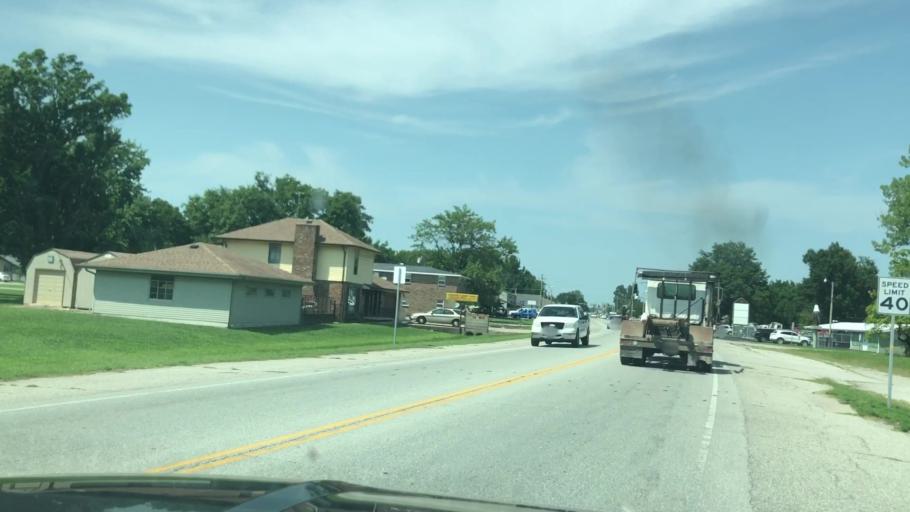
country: US
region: Oklahoma
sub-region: Ottawa County
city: Commerce
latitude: 36.9292
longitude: -94.8675
